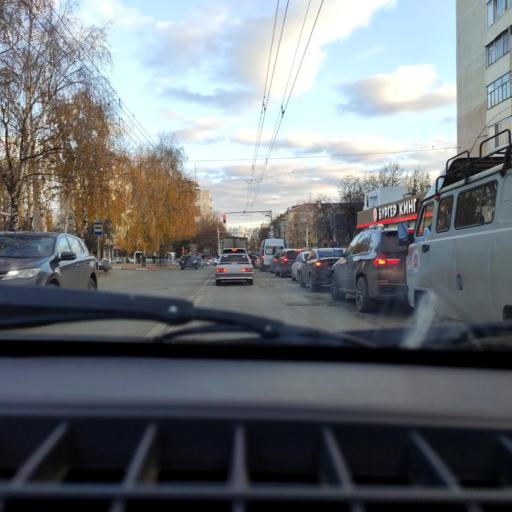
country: RU
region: Bashkortostan
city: Ufa
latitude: 54.7611
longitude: 56.0096
